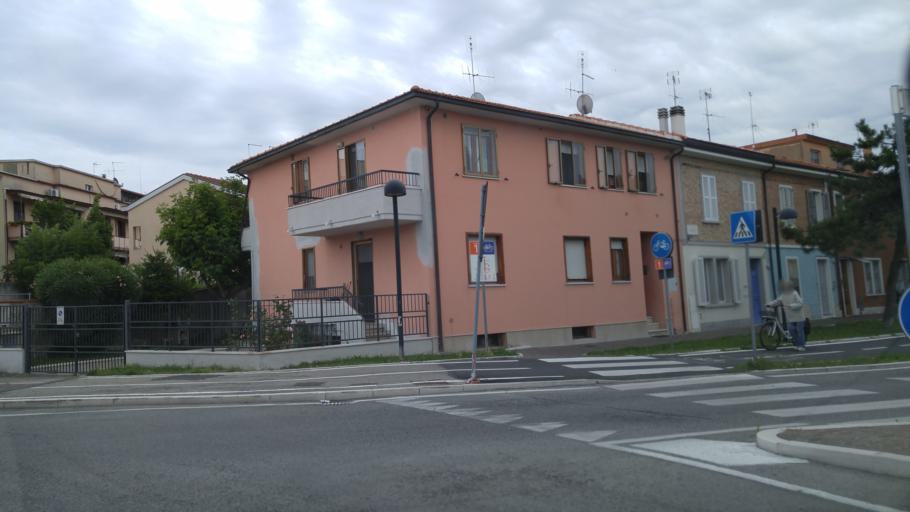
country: IT
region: The Marches
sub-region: Provincia di Pesaro e Urbino
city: Pesaro
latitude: 43.9161
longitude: 12.9043
